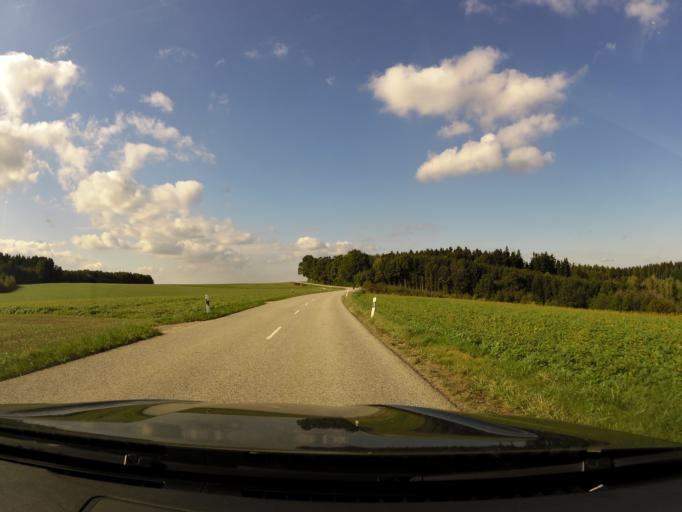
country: DE
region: Bavaria
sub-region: Lower Bavaria
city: Kumhausen
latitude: 48.4781
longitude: 12.1477
